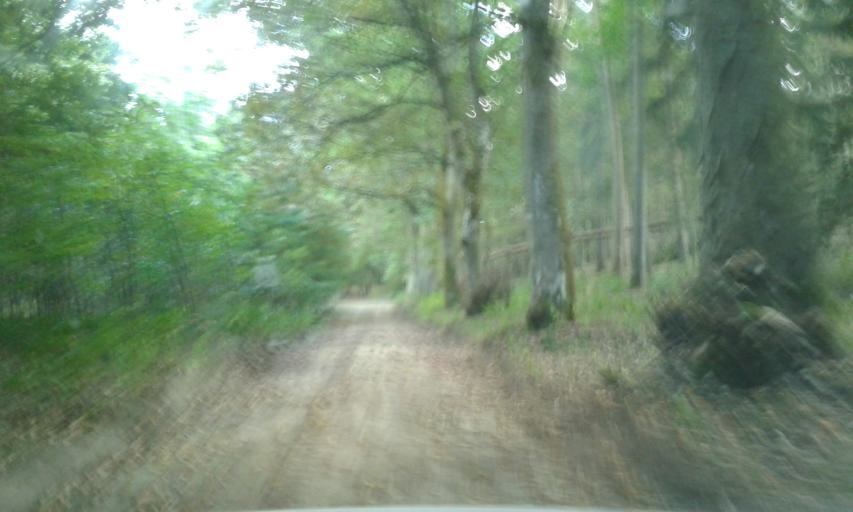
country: PL
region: West Pomeranian Voivodeship
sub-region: Powiat stargardzki
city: Dolice
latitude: 53.2273
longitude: 15.2542
